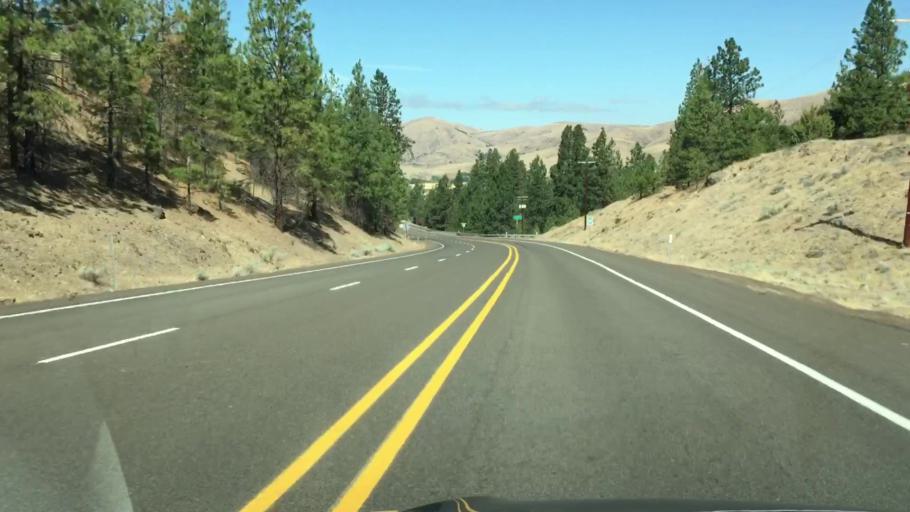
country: US
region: Oregon
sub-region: Wasco County
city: The Dalles
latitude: 45.2372
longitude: -121.1449
